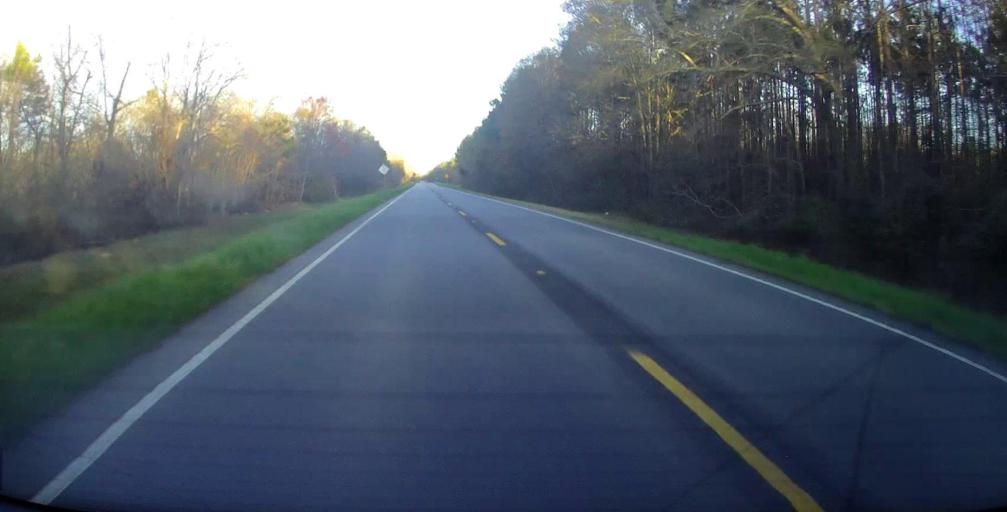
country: US
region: Georgia
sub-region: Wilcox County
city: Rochelle
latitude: 31.9499
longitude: -83.5673
